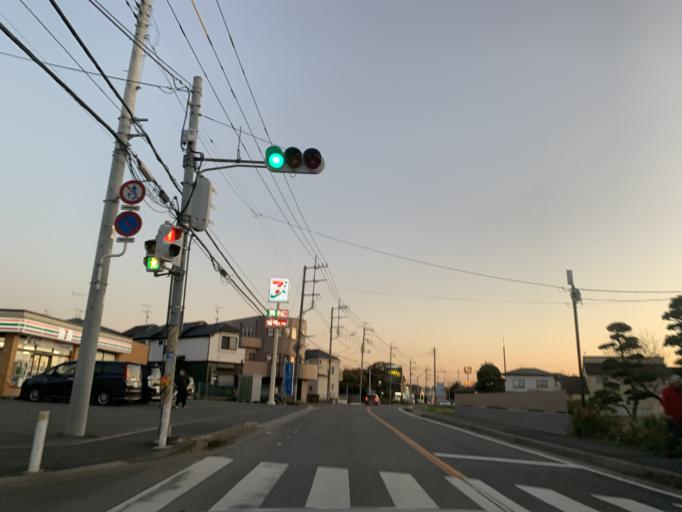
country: JP
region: Chiba
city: Nagareyama
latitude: 35.9012
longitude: 139.9022
